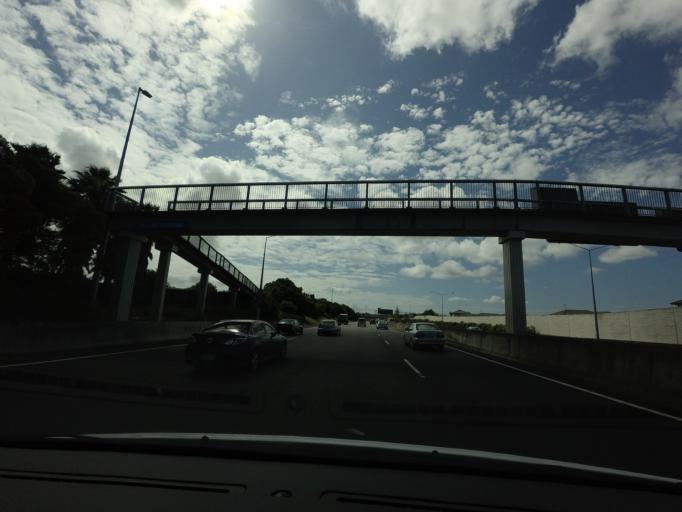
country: NZ
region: Auckland
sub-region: Auckland
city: Mangere
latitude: -36.9584
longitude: 174.7976
